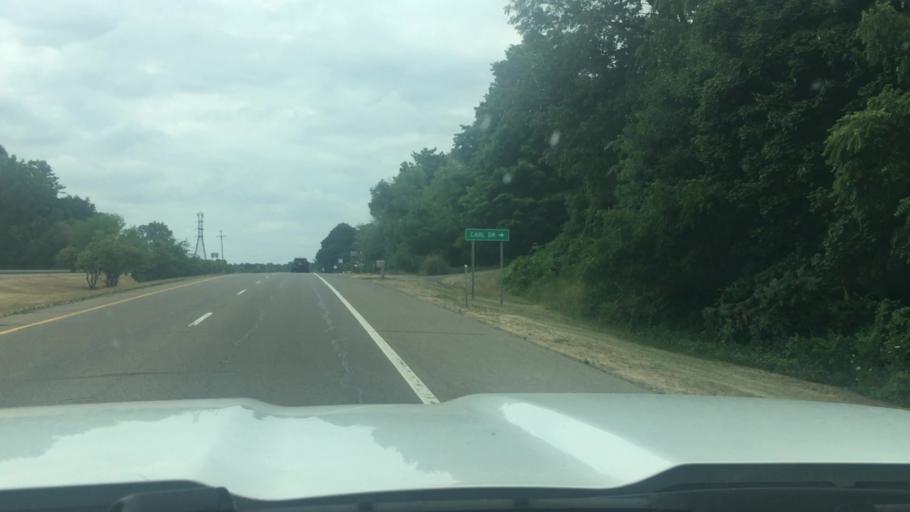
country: US
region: Michigan
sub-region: Kent County
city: Forest Hills
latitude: 42.9633
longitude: -85.5322
